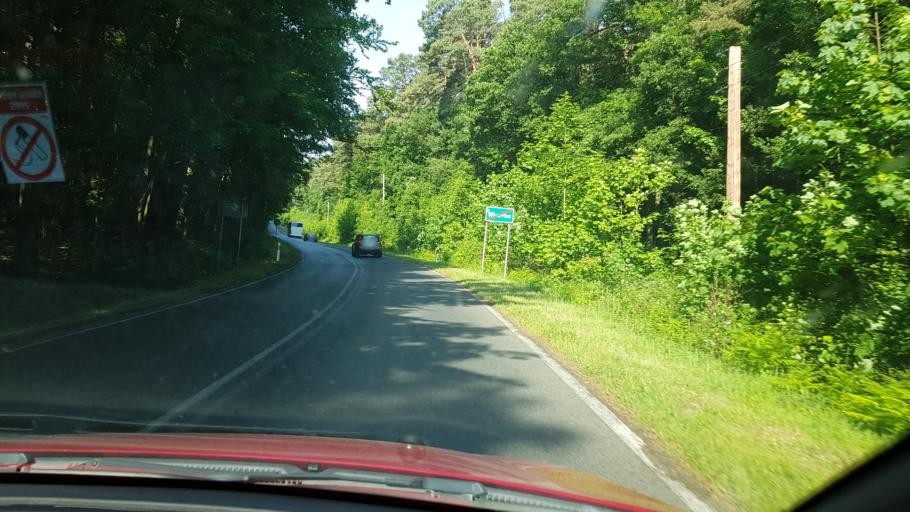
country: PL
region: West Pomeranian Voivodeship
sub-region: Powiat kamienski
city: Miedzyzdroje
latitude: 53.9663
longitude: 14.5584
